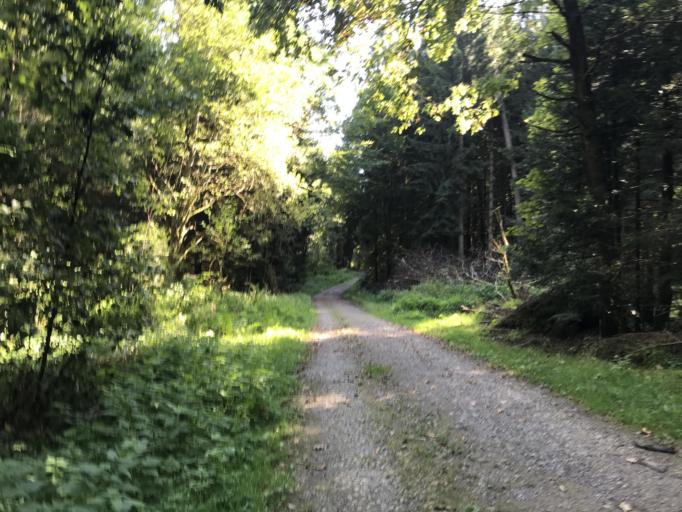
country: DE
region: Baden-Wuerttemberg
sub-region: Karlsruhe Region
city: Calw
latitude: 48.7030
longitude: 8.7249
